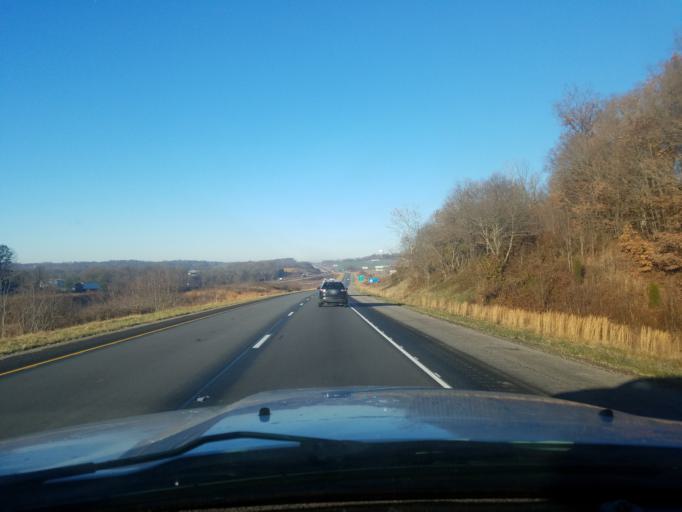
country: US
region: Indiana
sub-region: Dubois County
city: Ferdinand
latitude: 38.2028
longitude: -86.8337
